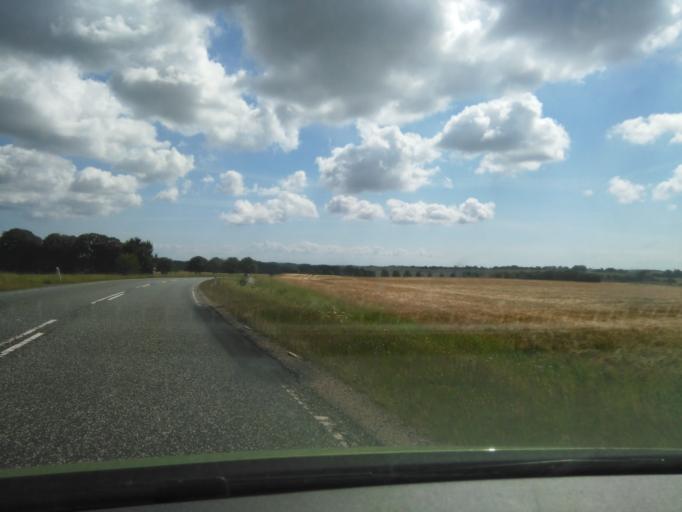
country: DK
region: Central Jutland
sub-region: Odder Kommune
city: Odder
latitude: 55.9668
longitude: 10.0865
